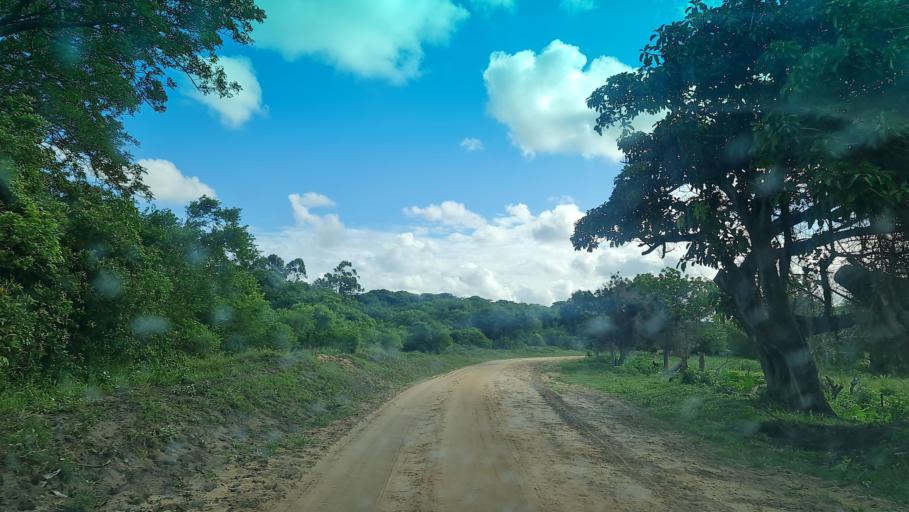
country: MZ
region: Maputo
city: Manhica
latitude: -25.4355
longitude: 32.8836
